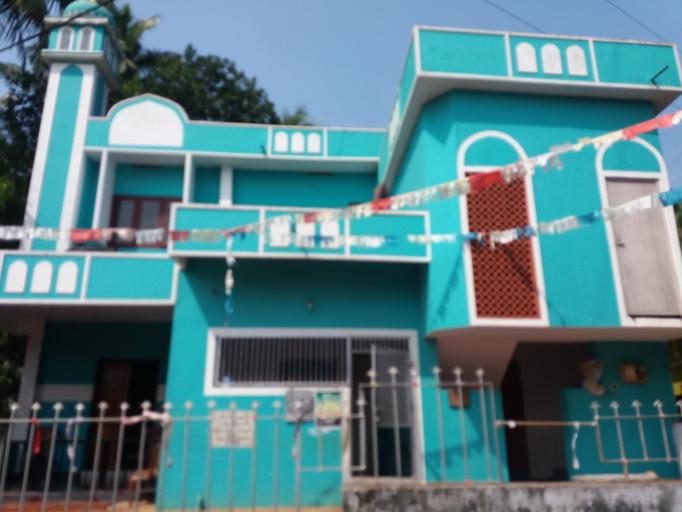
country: IN
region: Kerala
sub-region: Kozhikode
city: Kunnamangalam
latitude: 11.2974
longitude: 75.8191
